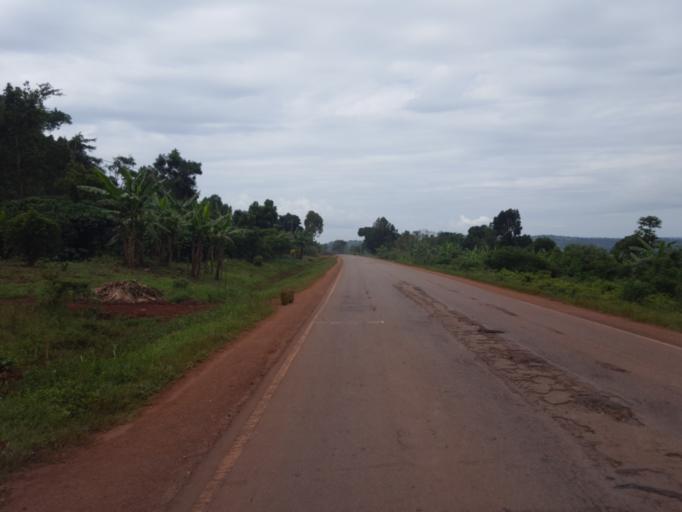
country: UG
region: Central Region
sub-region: Mityana District
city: Mityana
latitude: 0.6467
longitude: 32.0962
